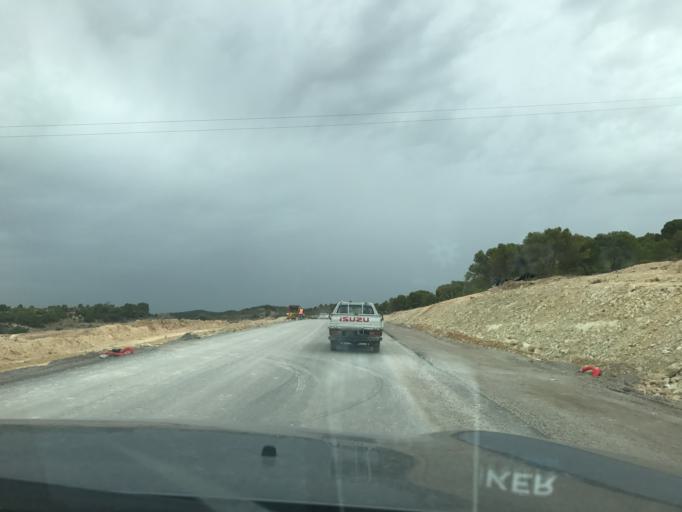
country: TN
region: Silyanah
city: Bu `Aradah
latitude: 36.2578
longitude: 9.7680
